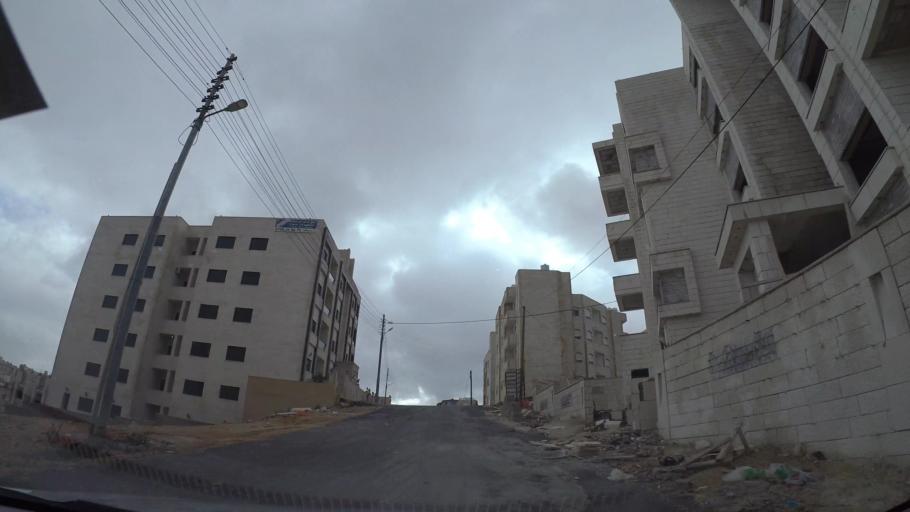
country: JO
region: Amman
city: Al Jubayhah
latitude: 32.0607
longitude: 35.8887
